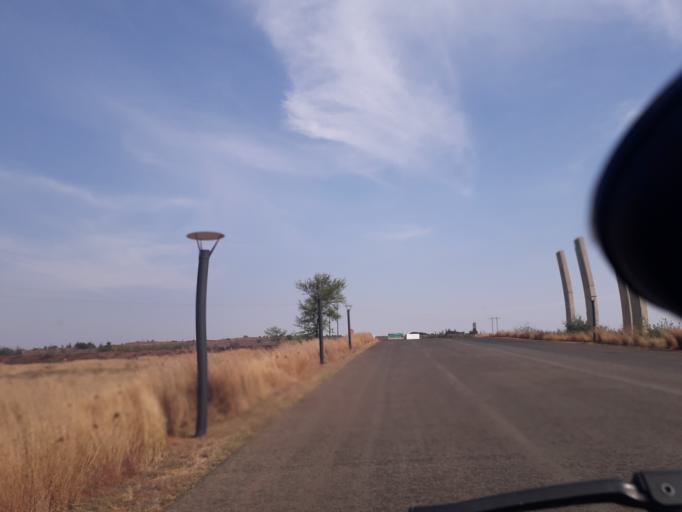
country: ZA
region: Gauteng
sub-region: West Rand District Municipality
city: Krugersdorp
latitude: -25.9779
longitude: 27.6643
